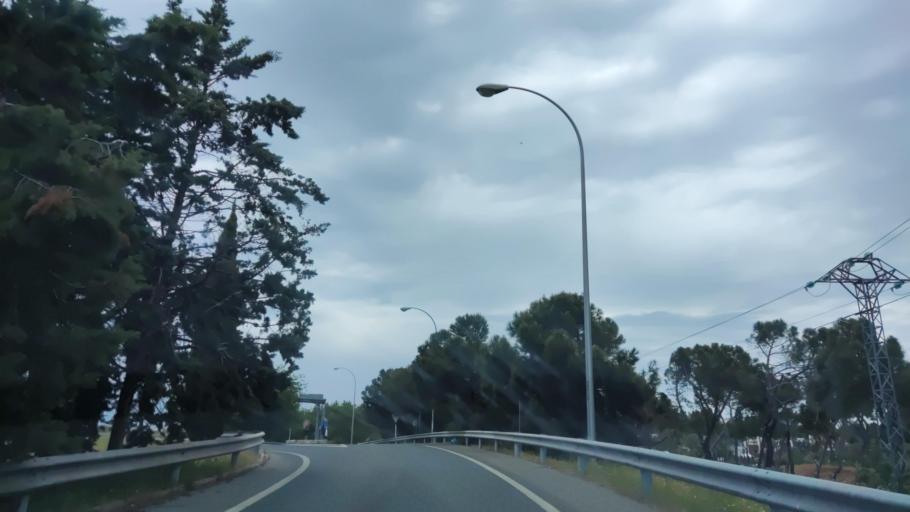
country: ES
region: Madrid
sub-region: Provincia de Madrid
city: Tetuan de las Victorias
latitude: 40.4687
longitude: -3.7490
